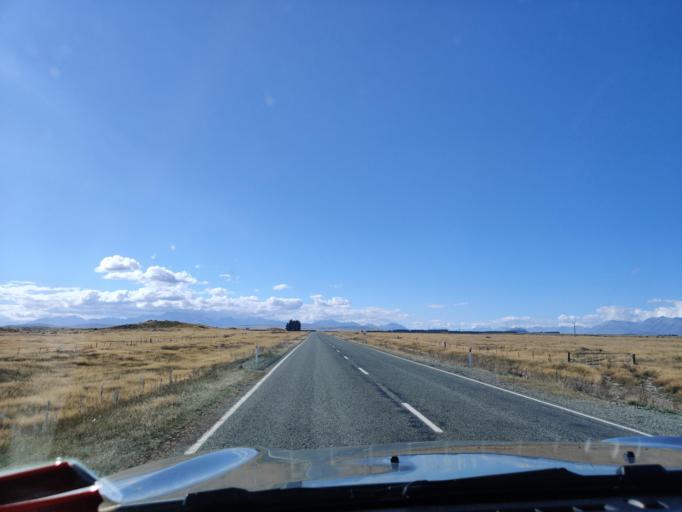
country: NZ
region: Canterbury
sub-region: Timaru District
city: Pleasant Point
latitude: -44.1312
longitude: 170.3497
